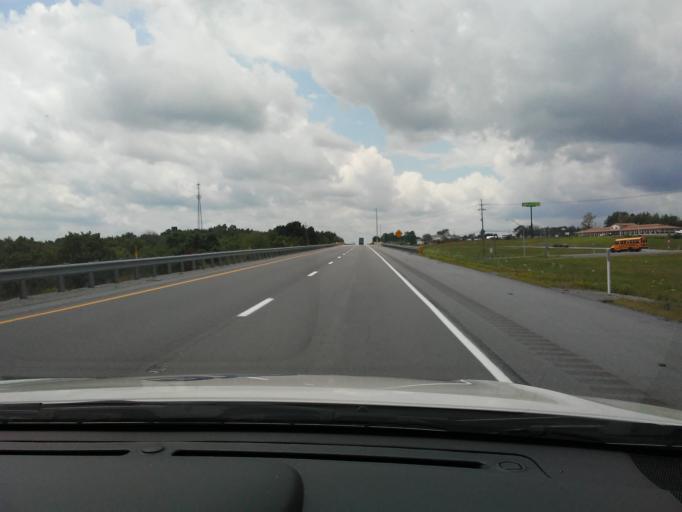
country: US
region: Pennsylvania
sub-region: Clearfield County
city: Troy
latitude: 40.9892
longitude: -78.1658
